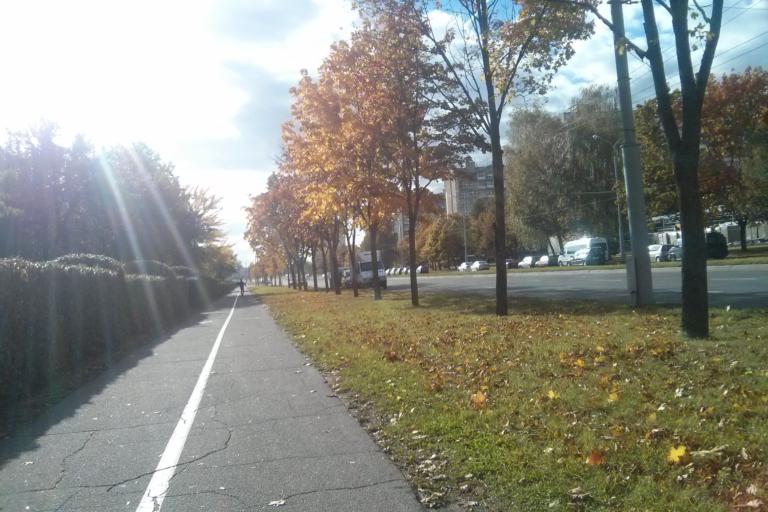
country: BY
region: Minsk
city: Minsk
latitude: 53.8507
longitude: 27.6092
